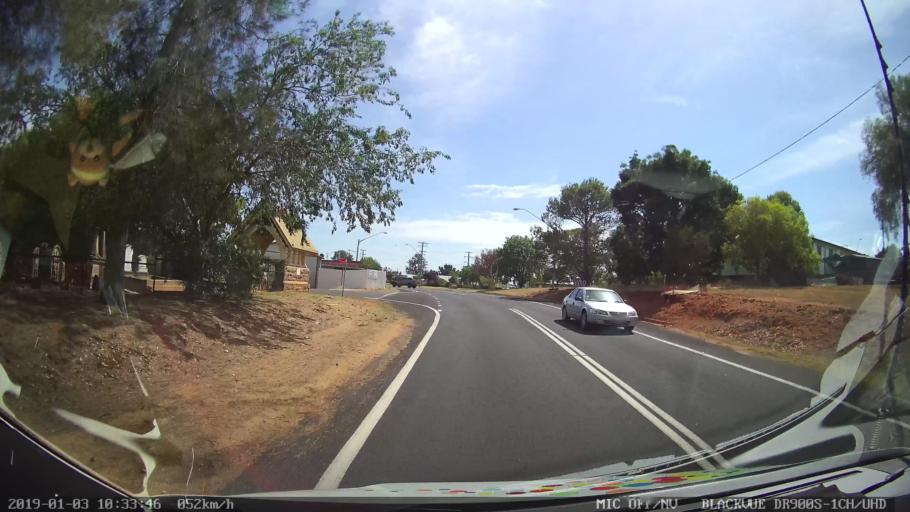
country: AU
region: New South Wales
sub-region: Young
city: Young
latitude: -34.3260
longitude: 148.2897
